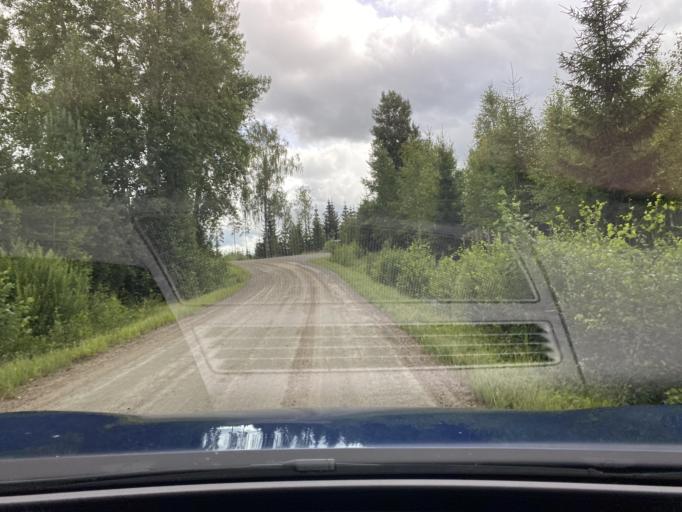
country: FI
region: Pirkanmaa
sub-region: Lounais-Pirkanmaa
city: Punkalaidun
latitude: 61.2122
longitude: 23.1693
